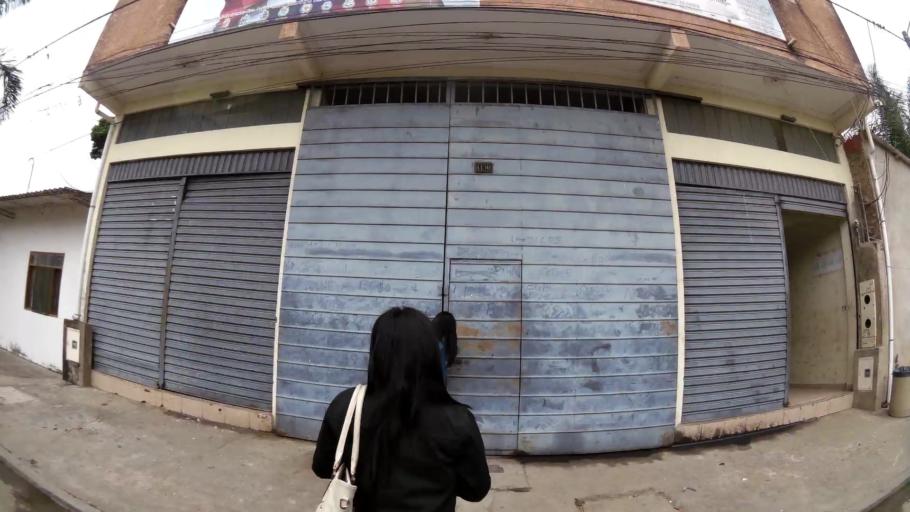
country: BO
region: Santa Cruz
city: Santa Cruz de la Sierra
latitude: -17.7741
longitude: -63.2133
